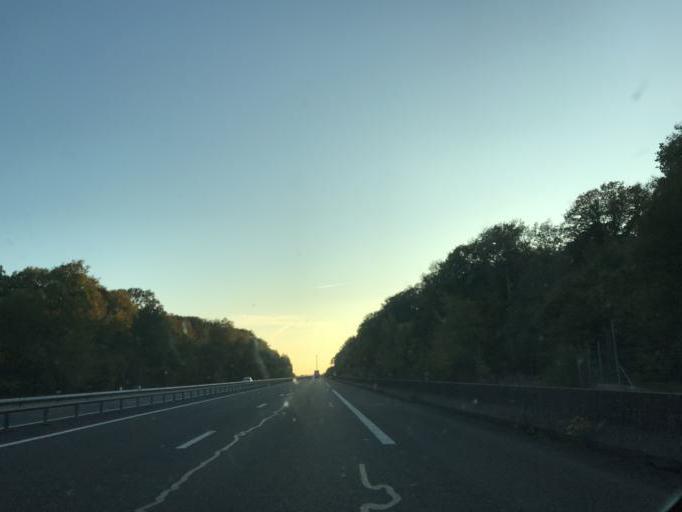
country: FR
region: Bourgogne
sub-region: Departement de l'Yonne
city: Paron
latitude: 48.1919
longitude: 3.1894
